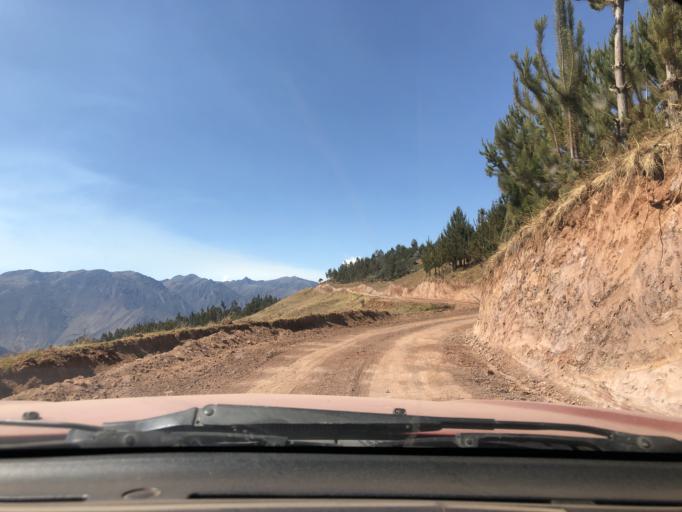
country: PE
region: Ayacucho
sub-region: Provincia de La Mar
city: Chilcas
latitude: -13.1822
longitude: -73.8437
